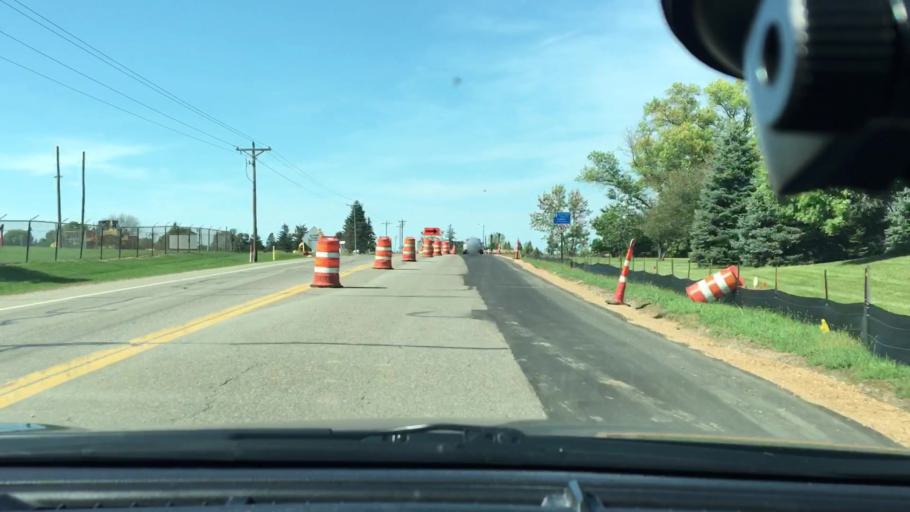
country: US
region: Minnesota
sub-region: Hennepin County
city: Corcoran
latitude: 45.0872
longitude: -93.5237
